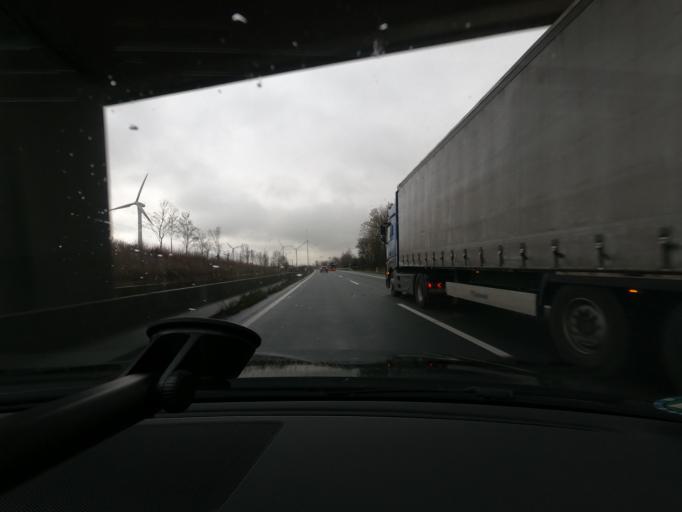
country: DE
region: North Rhine-Westphalia
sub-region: Regierungsbezirk Detmold
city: Wunnenberg
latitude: 51.5619
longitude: 8.7560
